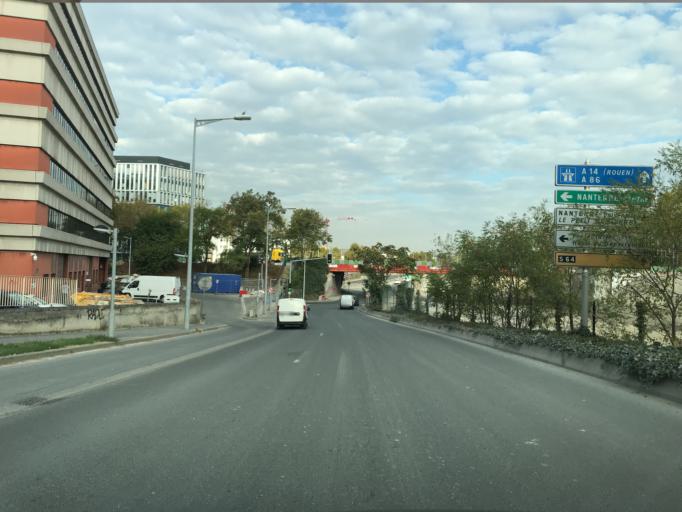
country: FR
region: Ile-de-France
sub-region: Departement des Hauts-de-Seine
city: Nanterre
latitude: 48.8980
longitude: 2.2223
